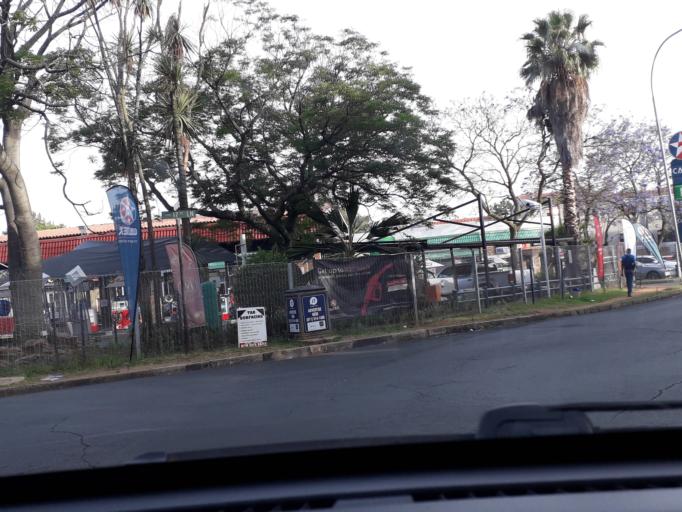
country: ZA
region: Gauteng
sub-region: City of Johannesburg Metropolitan Municipality
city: Johannesburg
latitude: -26.1479
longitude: 28.0625
